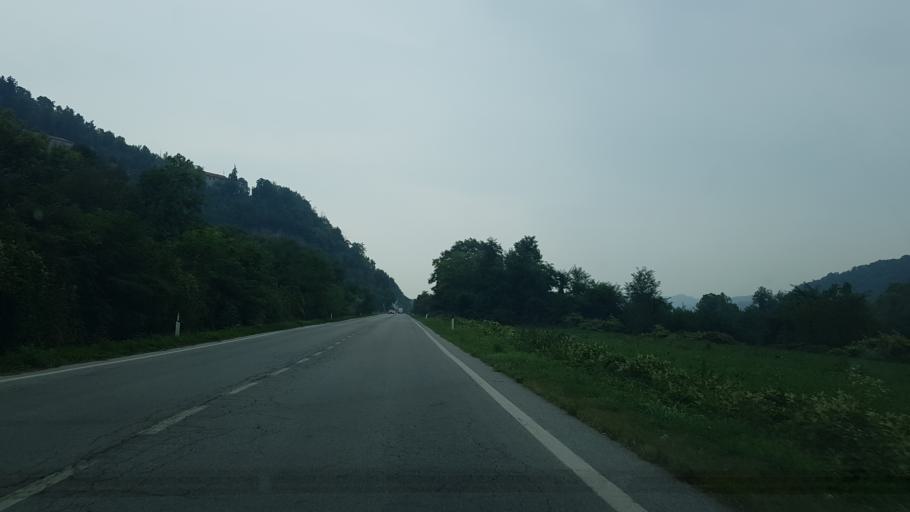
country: IT
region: Piedmont
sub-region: Provincia di Cuneo
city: Roccaforte Mondovi
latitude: 44.3289
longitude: 7.7514
